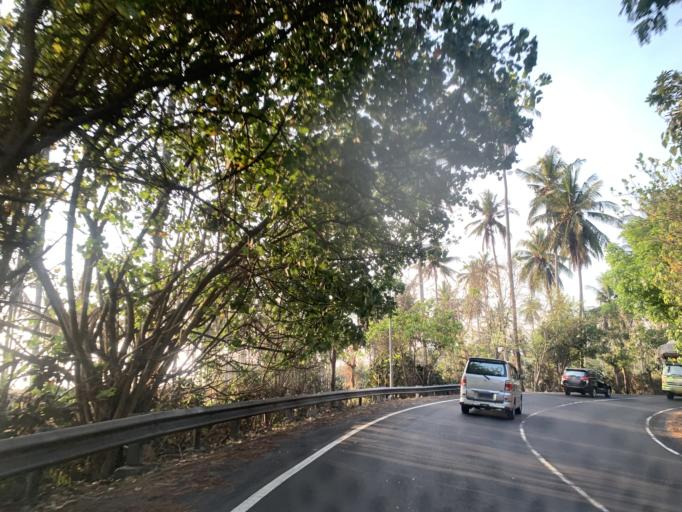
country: ID
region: Bali
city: Angkahgede
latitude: -8.4851
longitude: 114.9444
